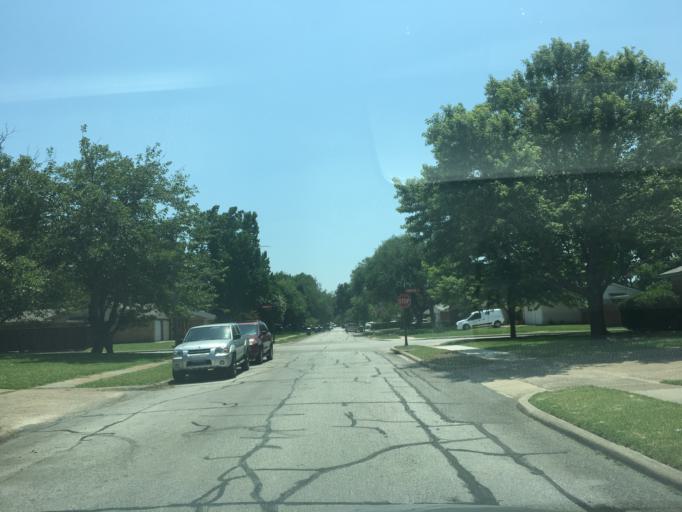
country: US
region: Texas
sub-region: Dallas County
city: Farmers Branch
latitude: 32.9336
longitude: -96.8803
